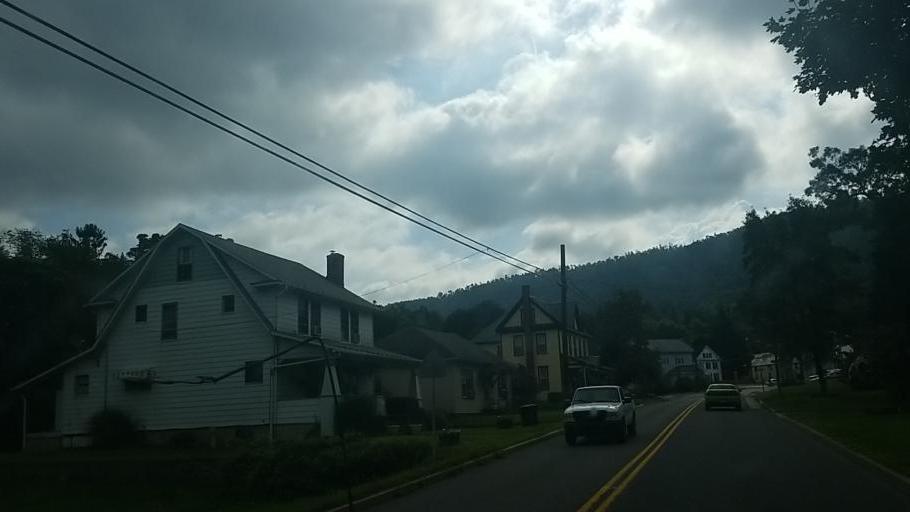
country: US
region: Pennsylvania
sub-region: Centre County
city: Pleasant Gap
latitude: 40.8658
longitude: -77.7364
